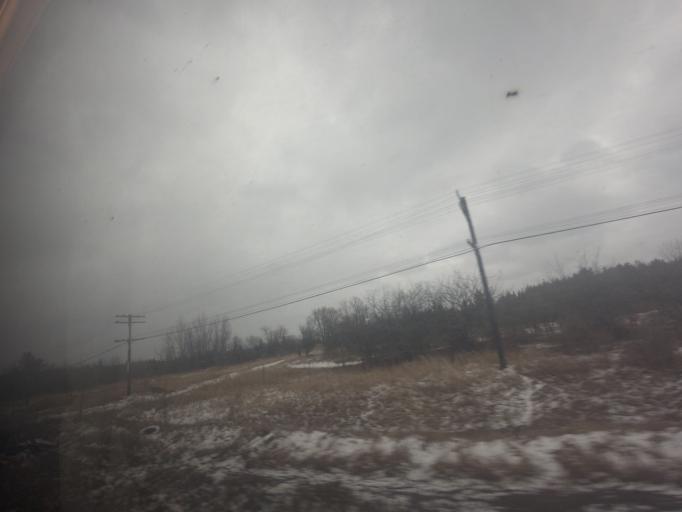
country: CA
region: Ontario
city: Cobourg
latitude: 43.9539
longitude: -78.2416
